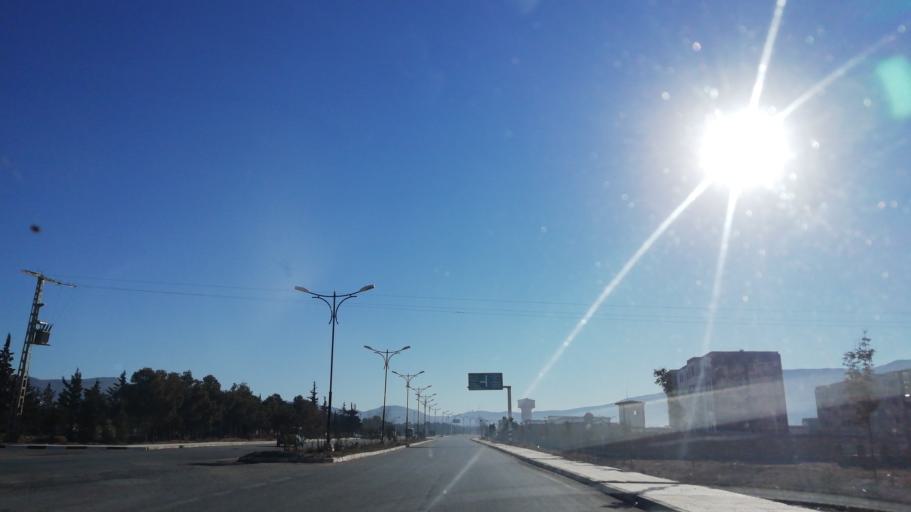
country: DZ
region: El Bayadh
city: El Bayadh
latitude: 33.6668
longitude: 1.0453
